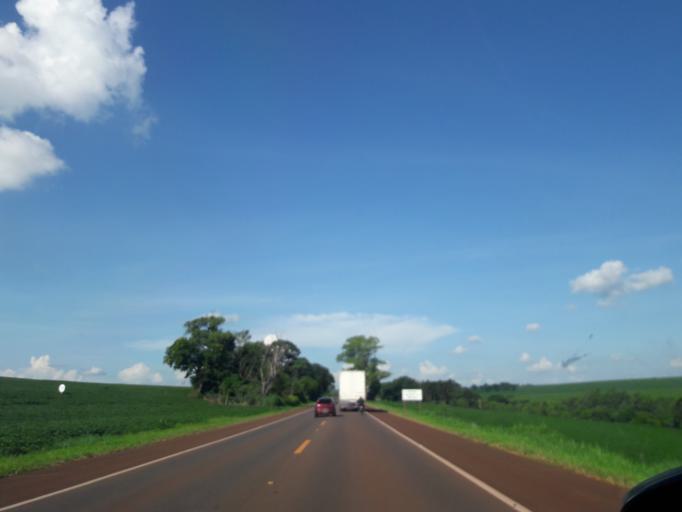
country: BR
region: Parana
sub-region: Campo Mourao
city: Campo Mourao
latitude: -24.3278
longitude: -52.6528
